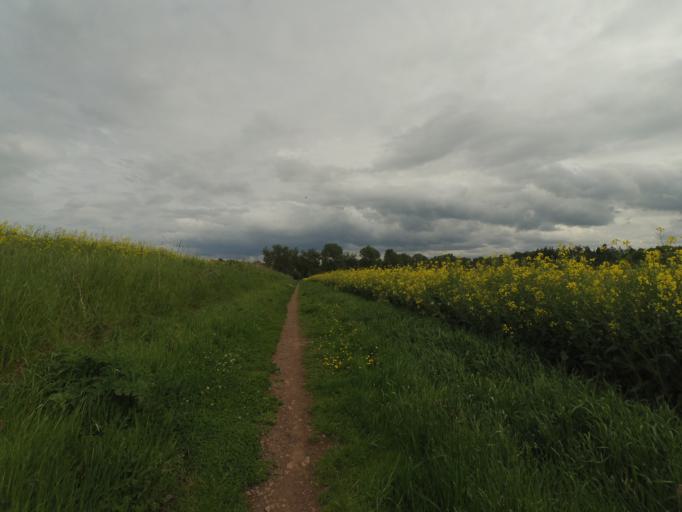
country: GB
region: Scotland
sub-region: East Lothian
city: Ormiston
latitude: 55.9136
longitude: -2.9266
